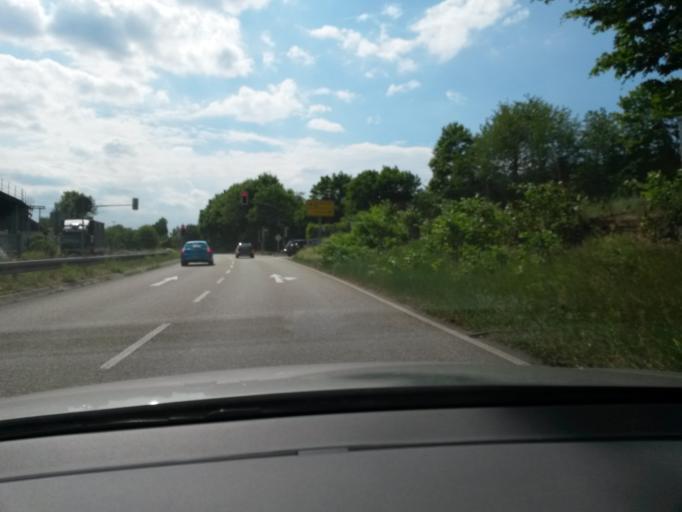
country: DE
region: Baden-Wuerttemberg
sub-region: Karlsruhe Region
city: Eutingen
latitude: 48.9043
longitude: 8.7371
